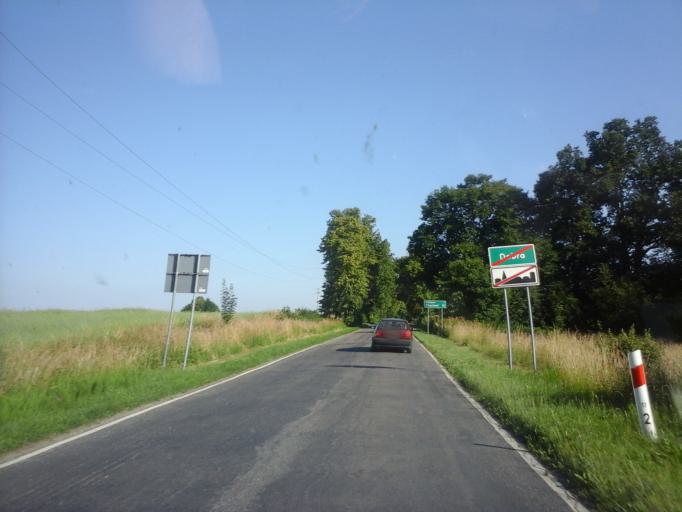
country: PL
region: West Pomeranian Voivodeship
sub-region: Powiat lobeski
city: Dobra
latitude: 53.5757
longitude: 15.3051
